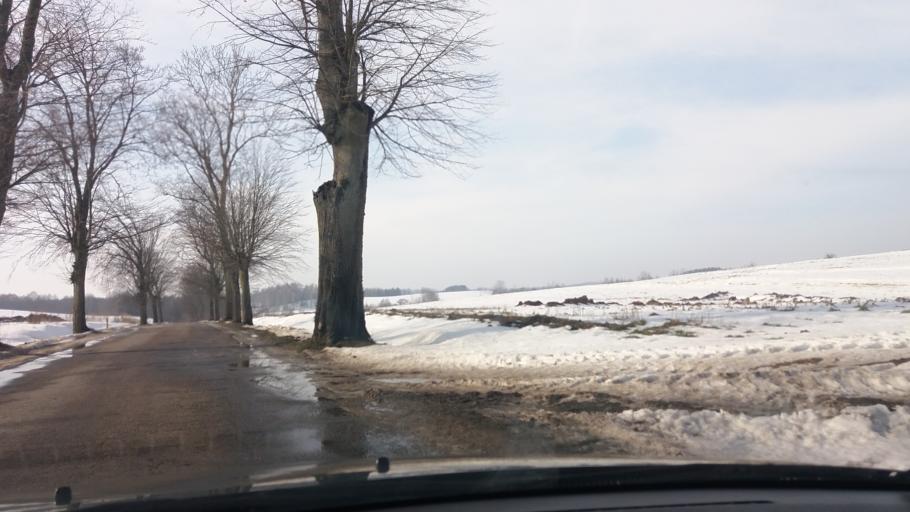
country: PL
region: Warmian-Masurian Voivodeship
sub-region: Powiat lidzbarski
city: Lidzbark Warminski
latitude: 54.1071
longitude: 20.6676
